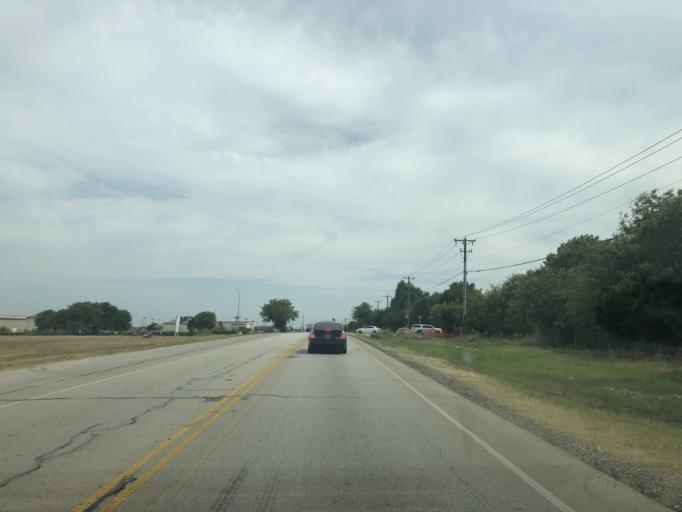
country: US
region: Texas
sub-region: Tarrant County
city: Blue Mound
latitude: 32.8751
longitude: -97.3425
